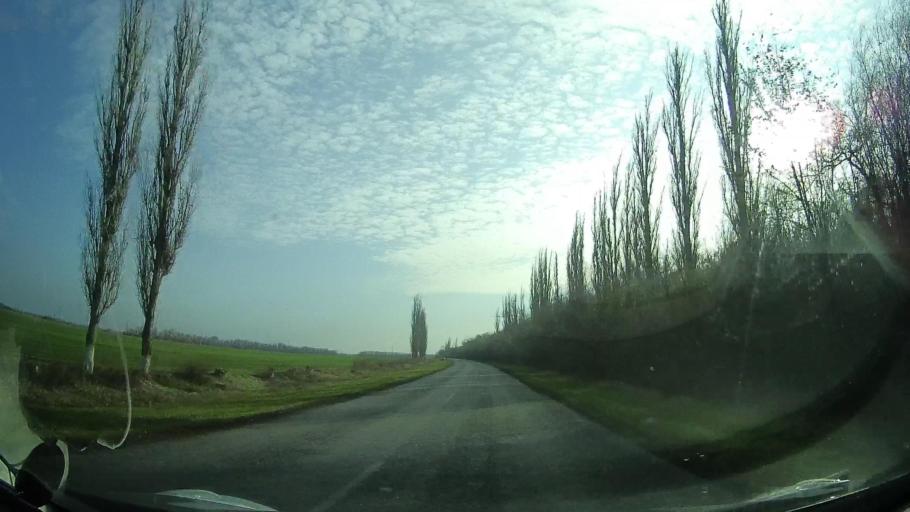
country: RU
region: Rostov
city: Mechetinskaya
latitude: 46.8233
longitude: 40.5541
